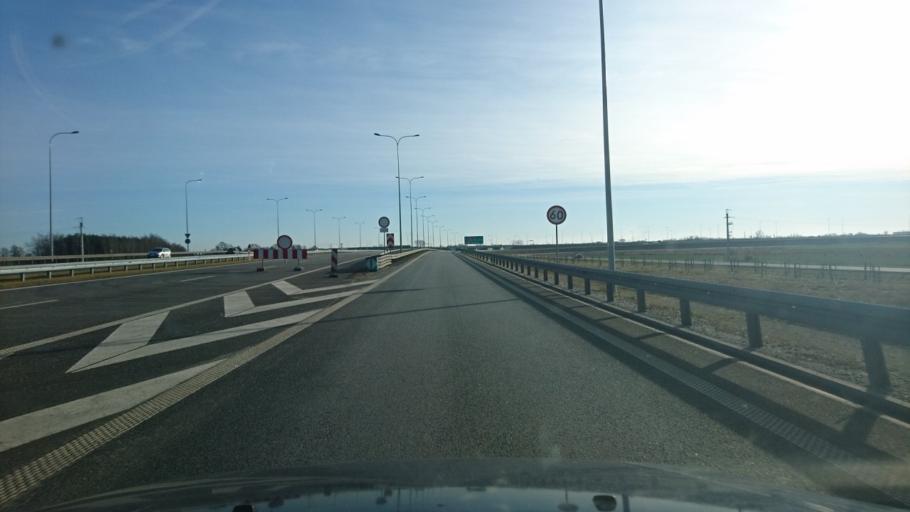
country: PL
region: Greater Poland Voivodeship
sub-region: Powiat kepinski
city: Kepno
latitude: 51.3208
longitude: 18.0032
